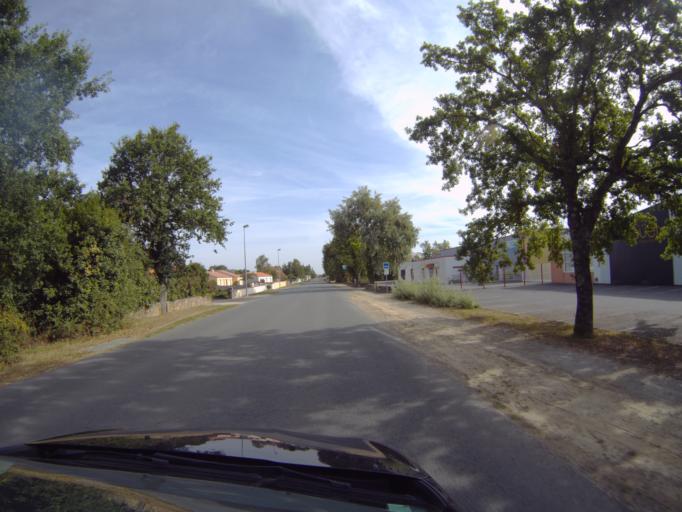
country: FR
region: Pays de la Loire
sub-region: Departement de la Vendee
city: Saint-Andre-Treize-Voies
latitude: 46.9017
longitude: -1.3808
